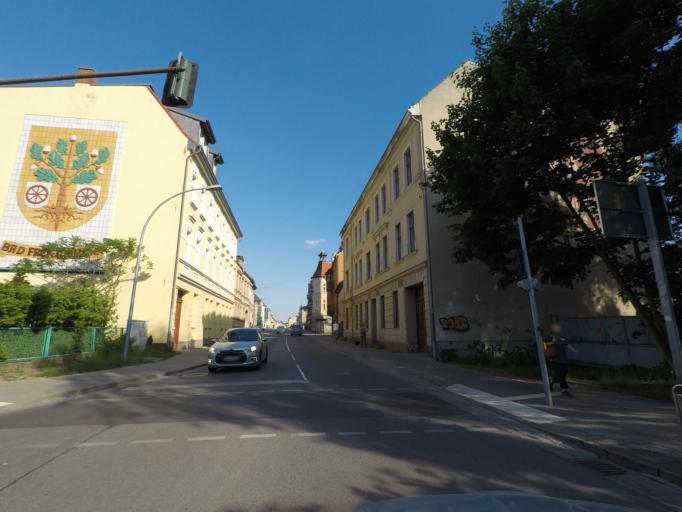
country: DE
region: Brandenburg
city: Bad Freienwalde
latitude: 52.7832
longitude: 14.0363
